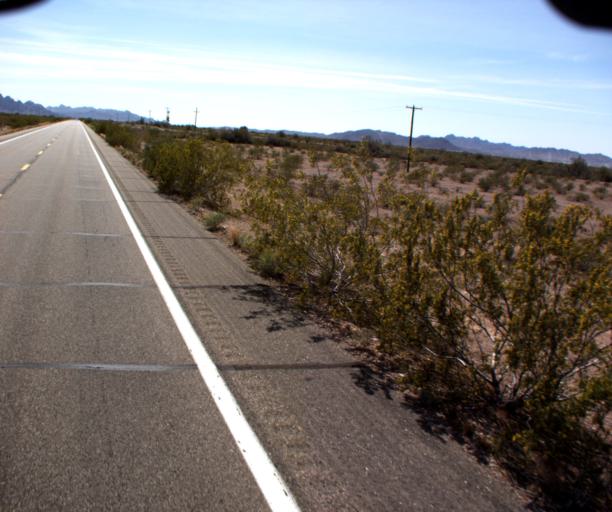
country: US
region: Arizona
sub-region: La Paz County
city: Quartzsite
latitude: 33.3835
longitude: -114.2172
